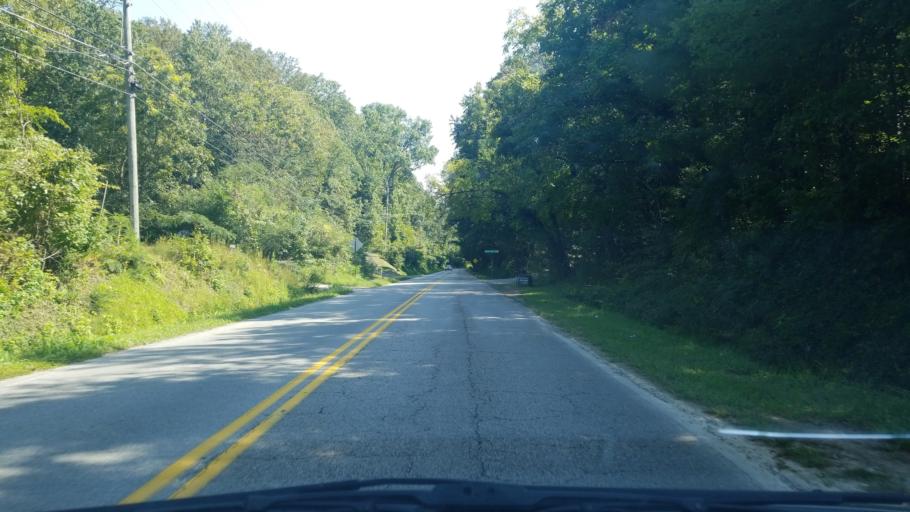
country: US
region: Tennessee
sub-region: Hamilton County
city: Collegedale
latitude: 35.0712
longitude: -85.0981
